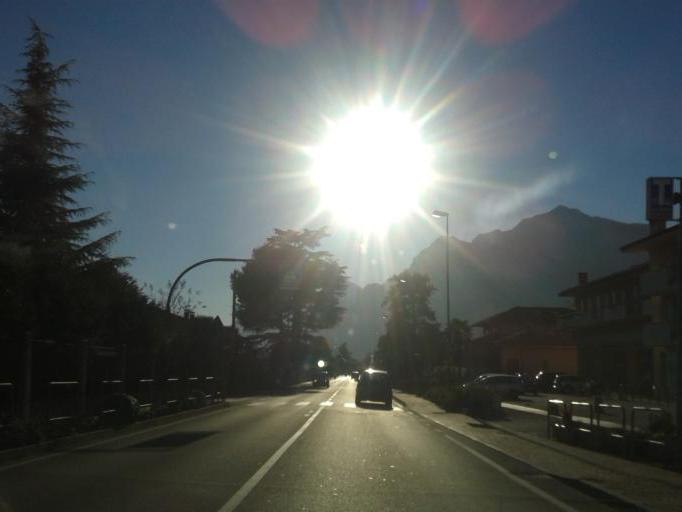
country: IT
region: Trentino-Alto Adige
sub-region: Provincia di Trento
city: Arco
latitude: 45.9148
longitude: 10.8779
